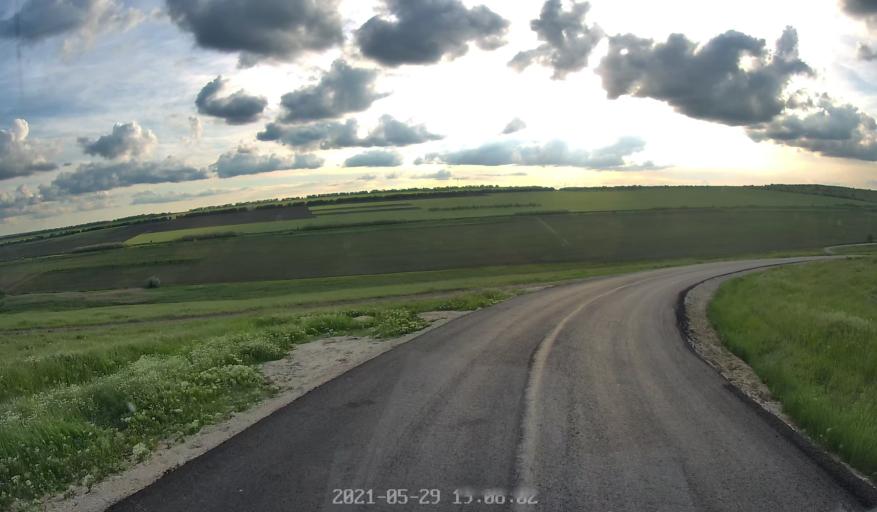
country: MD
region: Chisinau
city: Singera
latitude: 46.8260
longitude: 28.9616
